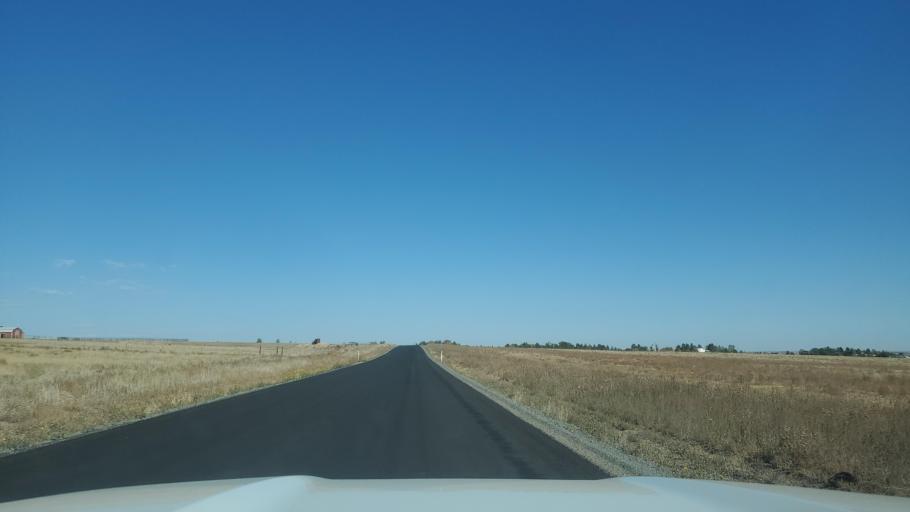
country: US
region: Colorado
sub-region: Adams County
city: Bennett
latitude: 39.7619
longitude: -104.3772
